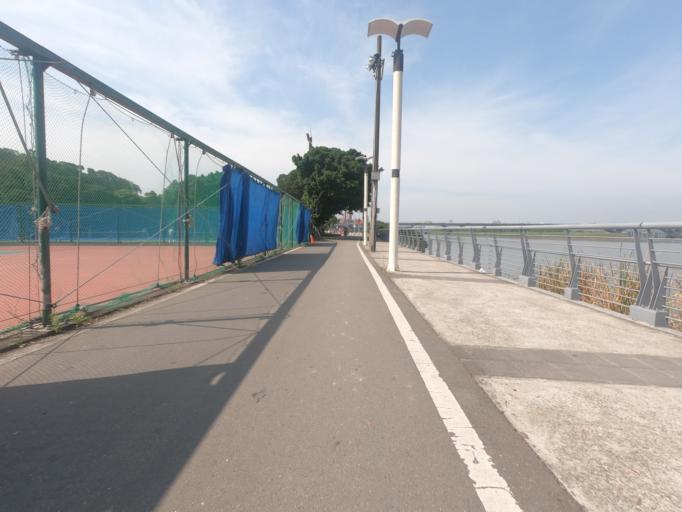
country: TW
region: Taipei
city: Taipei
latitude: 25.0550
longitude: 121.5067
